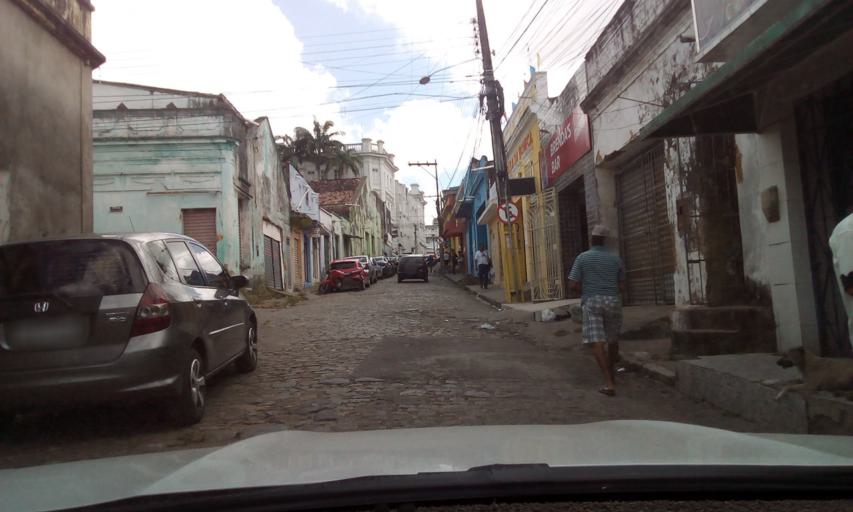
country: BR
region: Paraiba
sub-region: Joao Pessoa
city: Joao Pessoa
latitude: -7.1190
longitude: -34.8881
